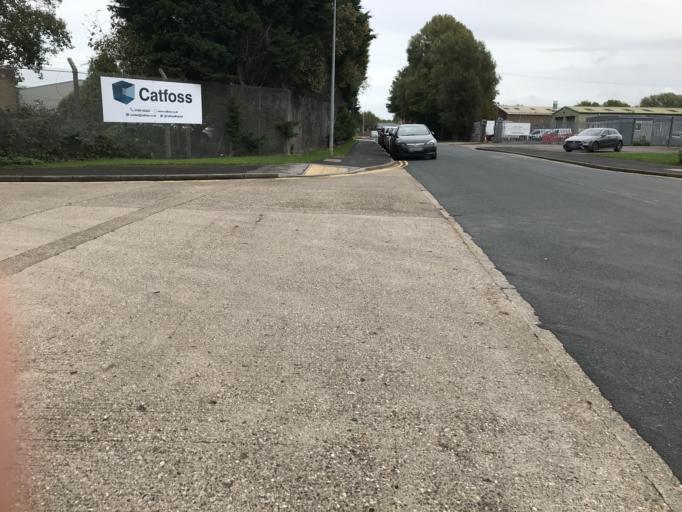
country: GB
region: England
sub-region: East Riding of Yorkshire
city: Beverley
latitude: 53.8405
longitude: -0.4032
